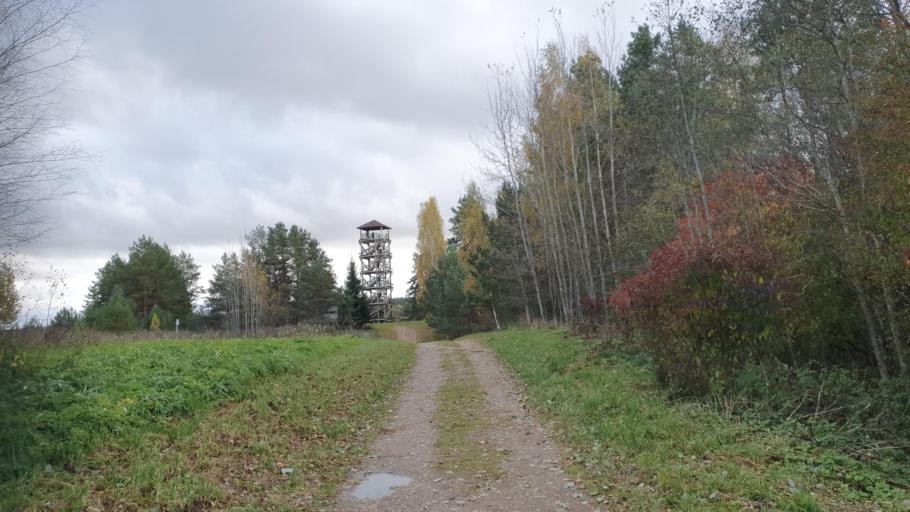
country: LV
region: Daugavpils
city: Daugavpils
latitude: 55.9161
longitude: 26.8148
